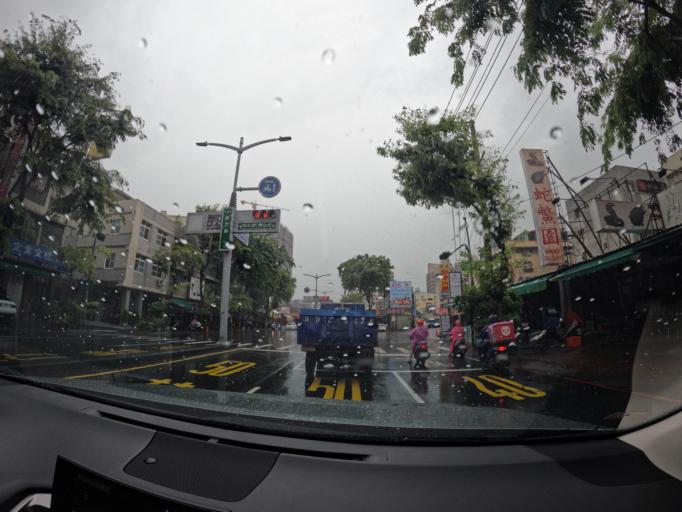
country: TW
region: Kaohsiung
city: Kaohsiung
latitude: 22.6610
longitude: 120.3220
